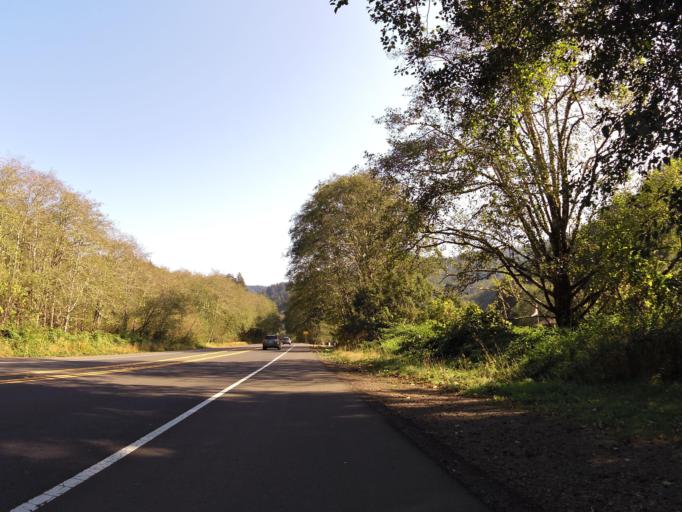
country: US
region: Oregon
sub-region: Tillamook County
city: Pacific City
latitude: 45.0942
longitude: -123.9759
